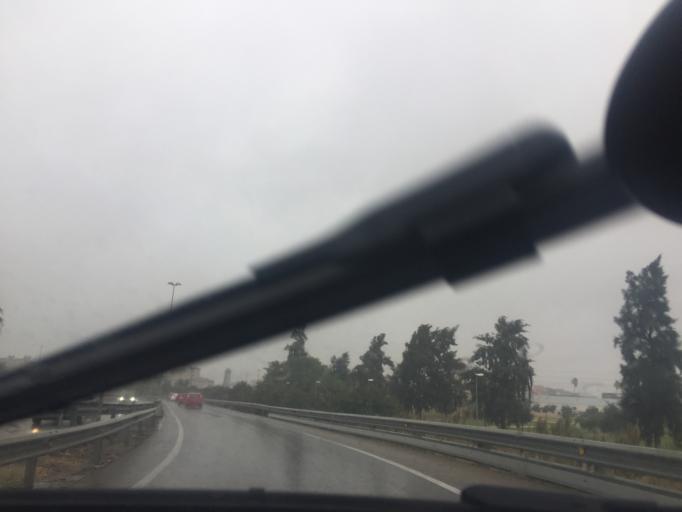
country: ES
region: Andalusia
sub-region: Provincia de Sevilla
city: Sevilla
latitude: 37.3611
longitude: -5.9543
